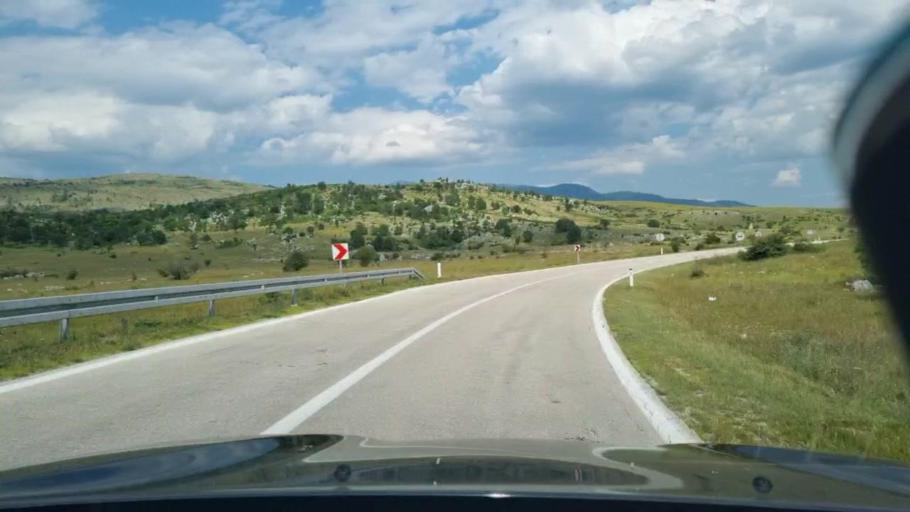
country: BA
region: Federation of Bosnia and Herzegovina
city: Bosansko Grahovo
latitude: 44.1323
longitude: 16.4838
